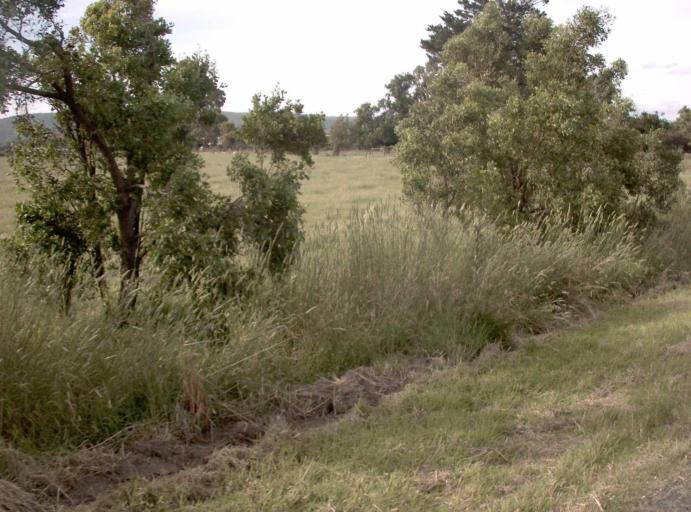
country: AU
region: Victoria
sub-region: Latrobe
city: Traralgon
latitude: -38.0989
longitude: 146.5956
